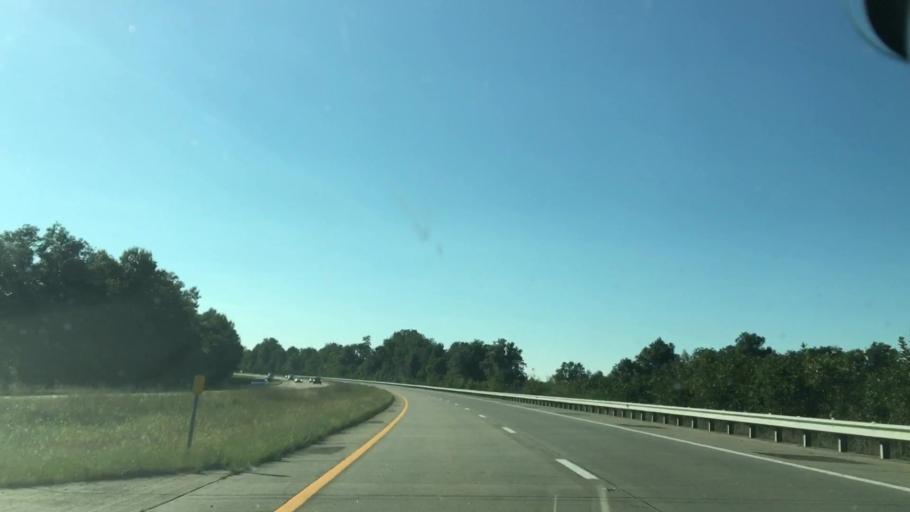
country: US
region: Kentucky
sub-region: Daviess County
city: Owensboro
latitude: 37.7623
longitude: -87.3049
